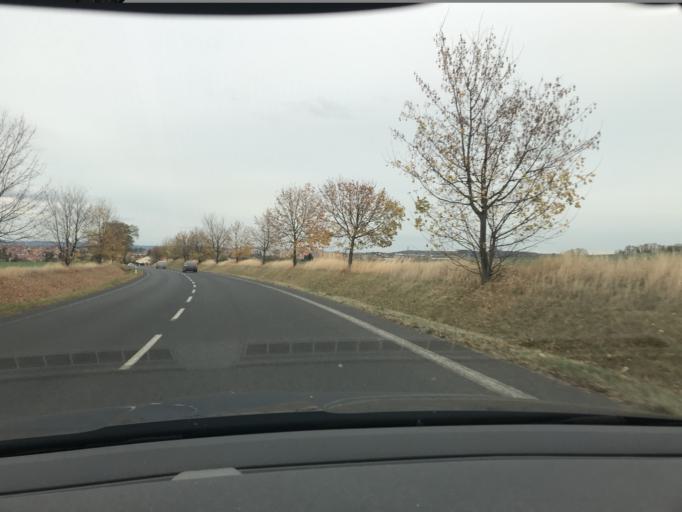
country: CZ
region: Ustecky
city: Roudnice nad Labem
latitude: 50.4179
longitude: 14.2160
